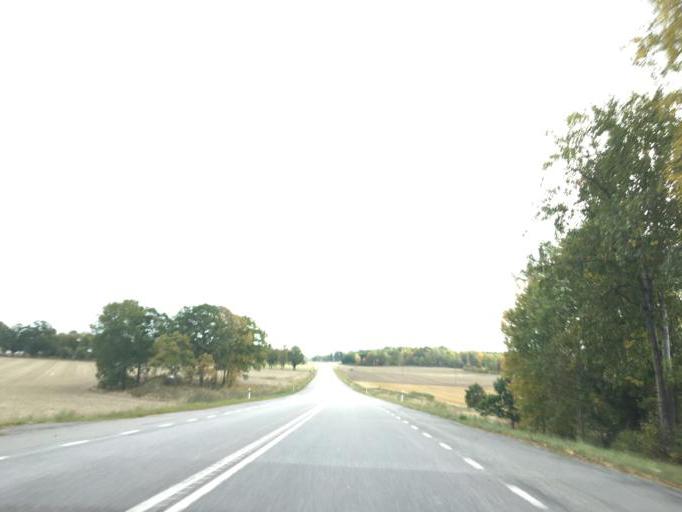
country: SE
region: Soedermanland
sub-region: Nykopings Kommun
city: Stigtomta
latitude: 58.8375
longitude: 16.7447
